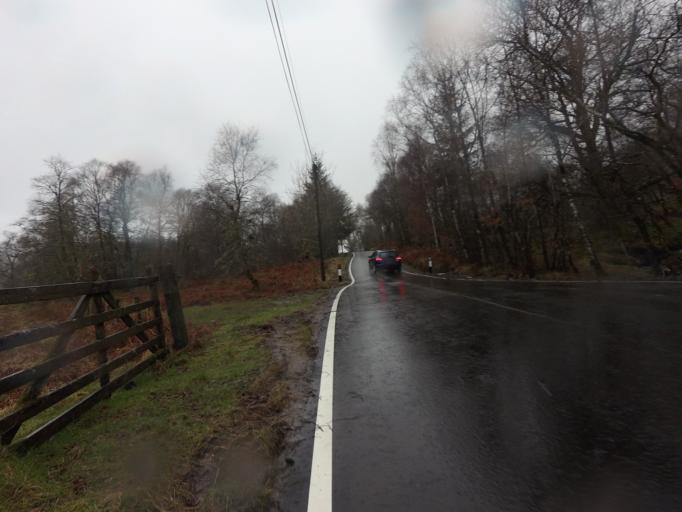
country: GB
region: Scotland
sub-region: West Dunbartonshire
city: Balloch
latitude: 56.1958
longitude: -4.5189
